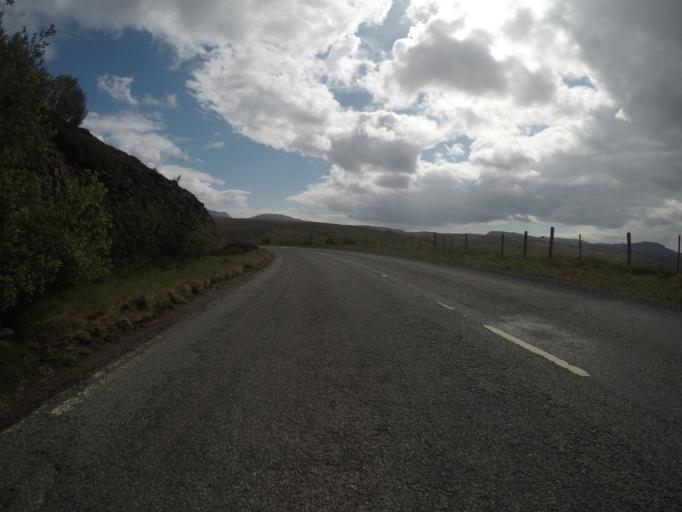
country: GB
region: Scotland
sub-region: Highland
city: Isle of Skye
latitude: 57.3036
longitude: -6.2996
